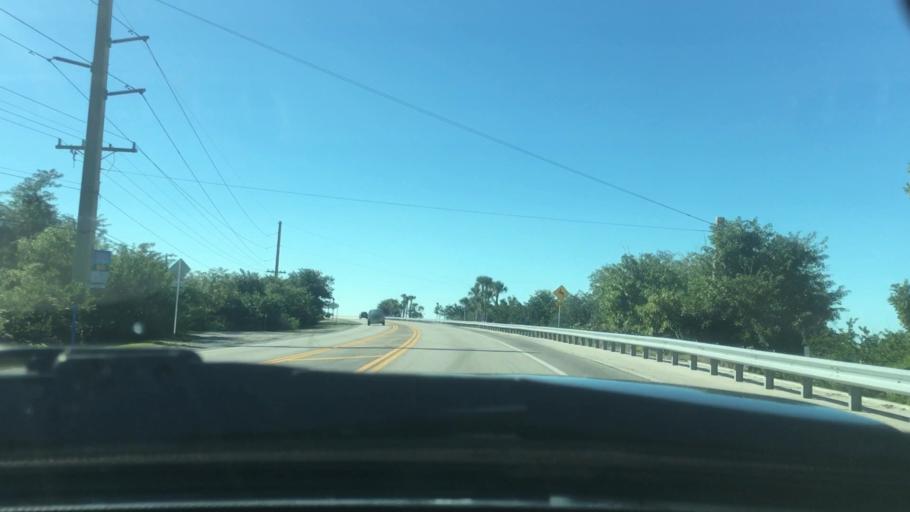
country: US
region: Florida
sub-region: Monroe County
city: Big Pine Key
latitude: 24.6698
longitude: -81.3696
